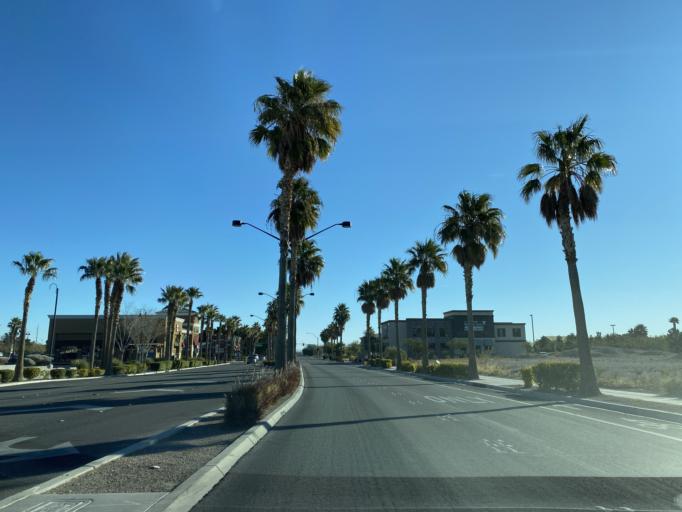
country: US
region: Nevada
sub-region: Clark County
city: Las Vegas
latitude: 36.2736
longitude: -115.2542
